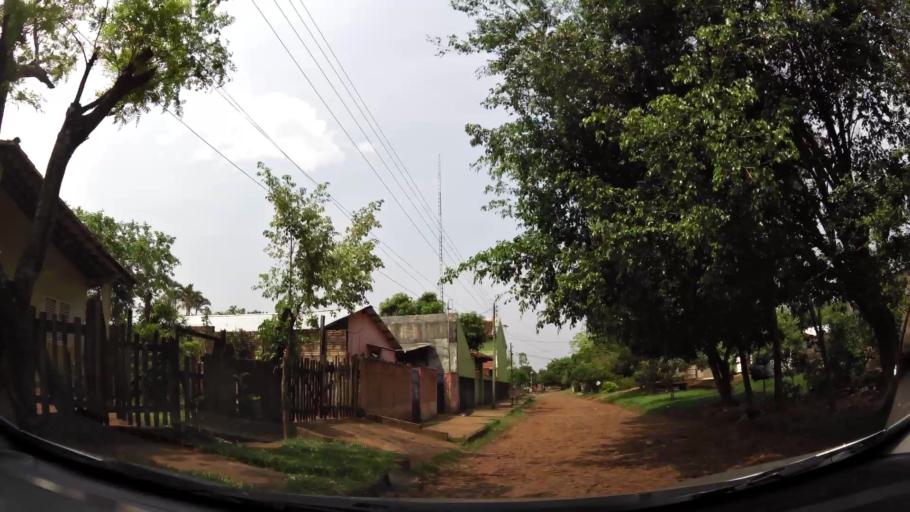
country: PY
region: Alto Parana
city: Presidente Franco
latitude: -25.5434
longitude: -54.6306
